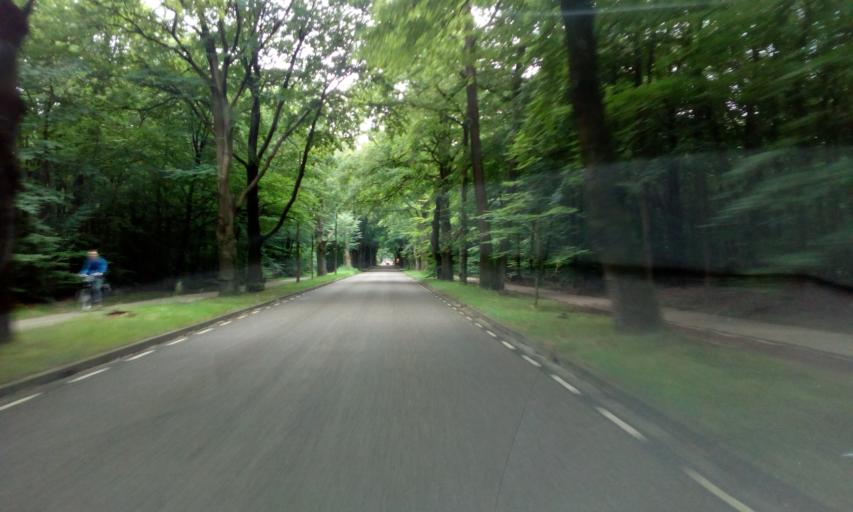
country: NL
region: North Holland
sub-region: Gemeente Hilversum
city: Hilversum
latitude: 52.2458
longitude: 5.1613
